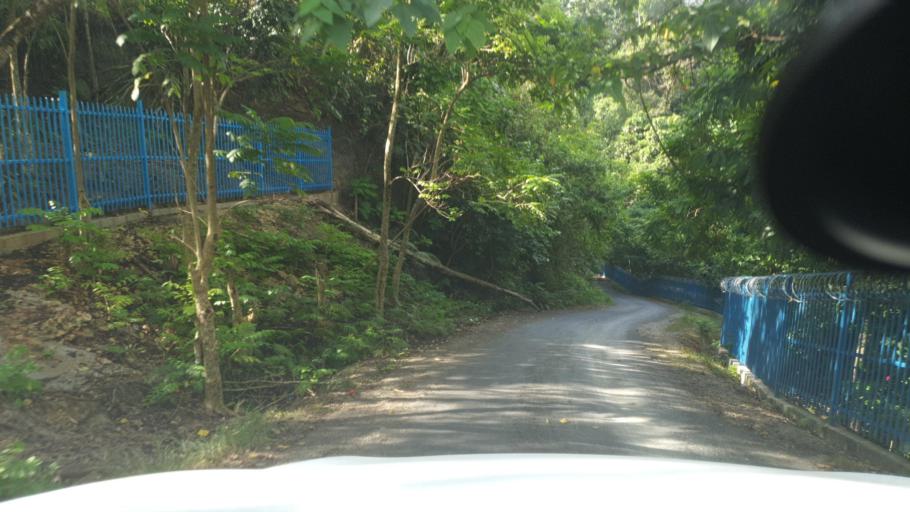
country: SB
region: Guadalcanal
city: Honiara
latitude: -9.4399
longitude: 159.9391
